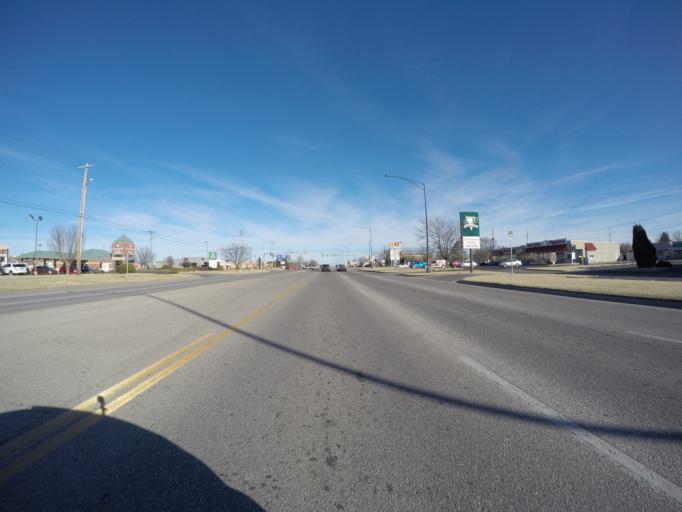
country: US
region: Kansas
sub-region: Sedgwick County
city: Maize
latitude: 37.7230
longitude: -97.4459
